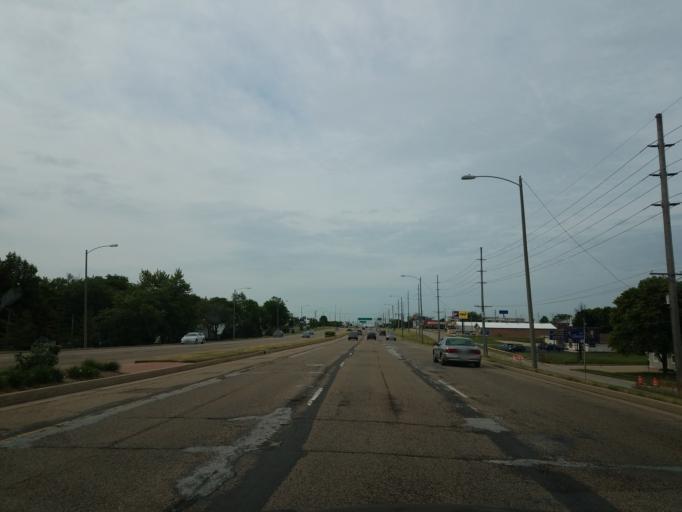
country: US
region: Illinois
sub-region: McLean County
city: Bloomington
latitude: 40.4950
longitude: -88.9531
